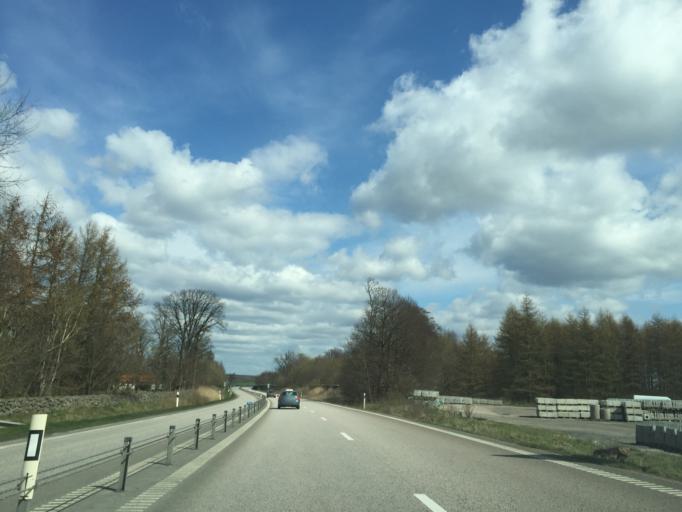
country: SE
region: Skane
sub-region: Horby Kommun
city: Hoerby
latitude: 55.8481
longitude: 13.6001
